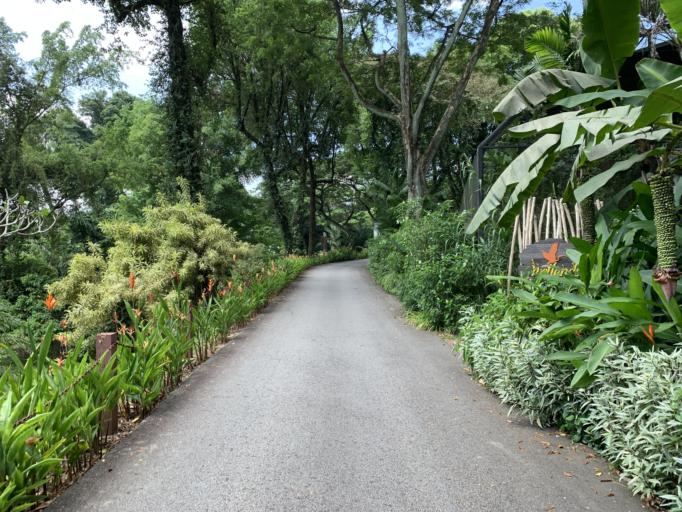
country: SG
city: Singapore
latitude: 1.3198
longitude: 103.7074
